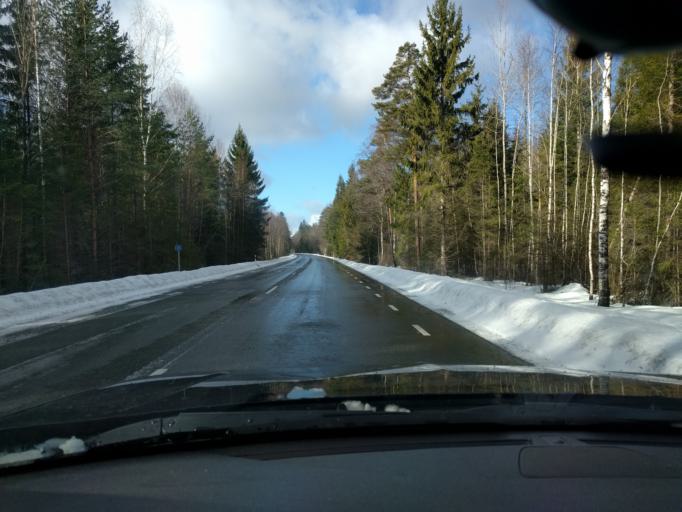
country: EE
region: Harju
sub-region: Kuusalu vald
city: Kuusalu
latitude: 59.2096
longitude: 25.5440
